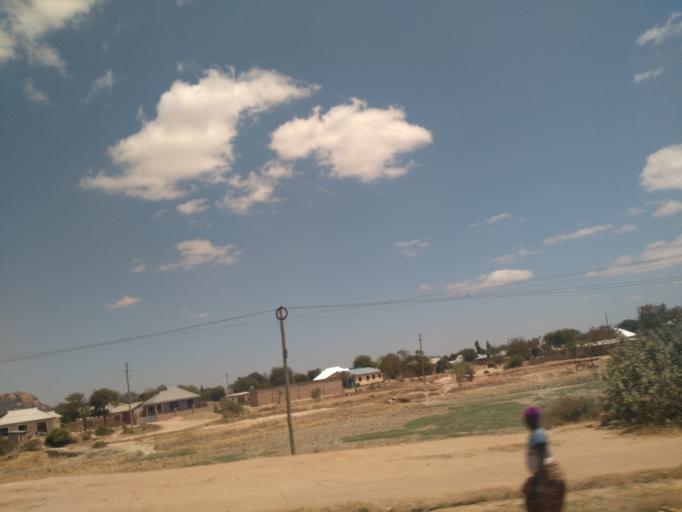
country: TZ
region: Dodoma
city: Kisasa
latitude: -6.1650
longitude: 35.7864
